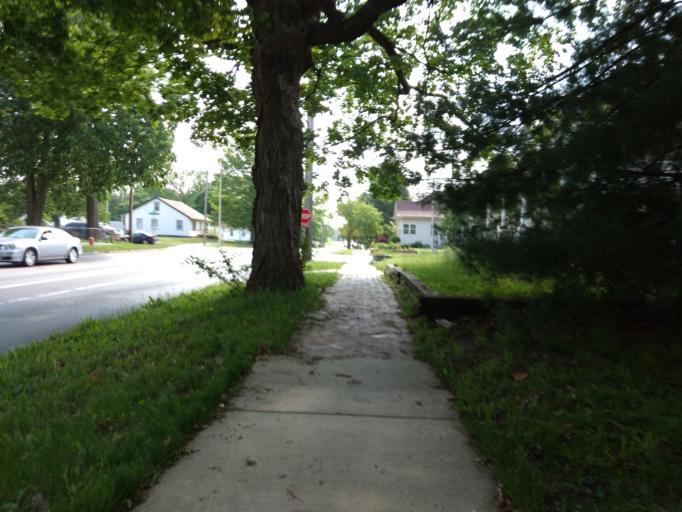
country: US
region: Illinois
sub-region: Champaign County
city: Urbana
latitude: 40.1129
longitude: -88.1964
